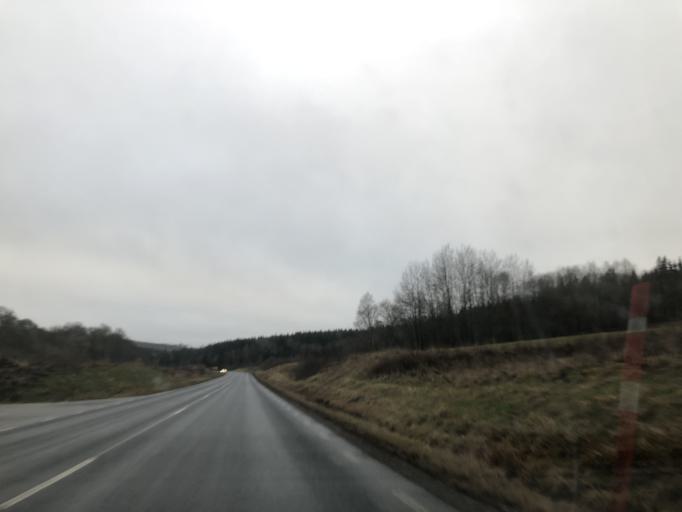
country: SE
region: Vaestra Goetaland
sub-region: Ulricehamns Kommun
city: Ulricehamn
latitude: 57.8259
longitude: 13.2887
